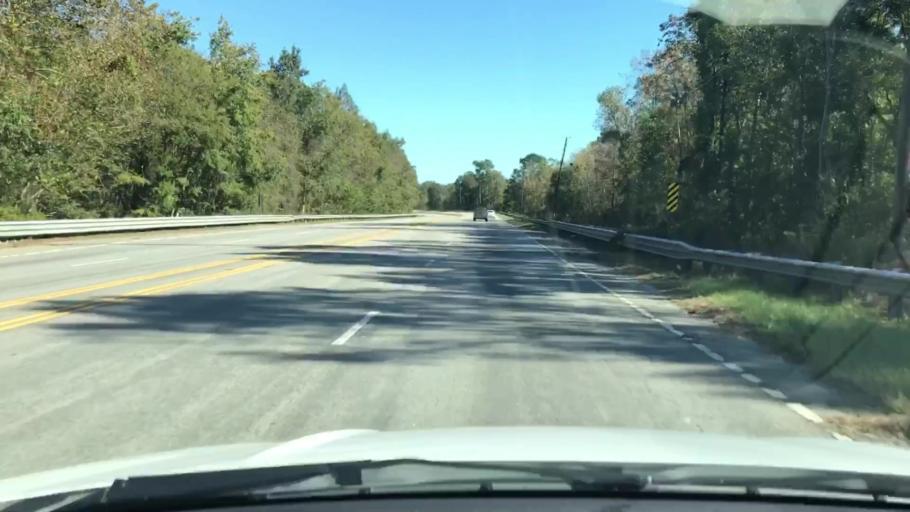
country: US
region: South Carolina
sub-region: Charleston County
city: Ravenel
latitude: 32.7636
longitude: -80.4433
